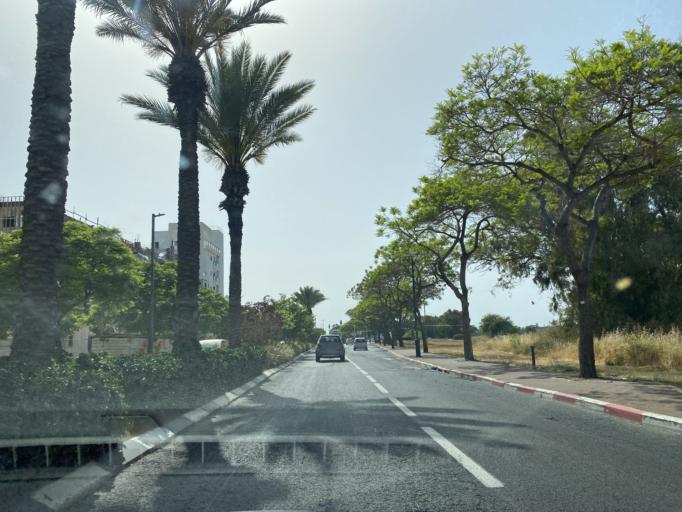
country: IL
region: Tel Aviv
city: Herzliyya
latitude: 32.1772
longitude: 34.8419
